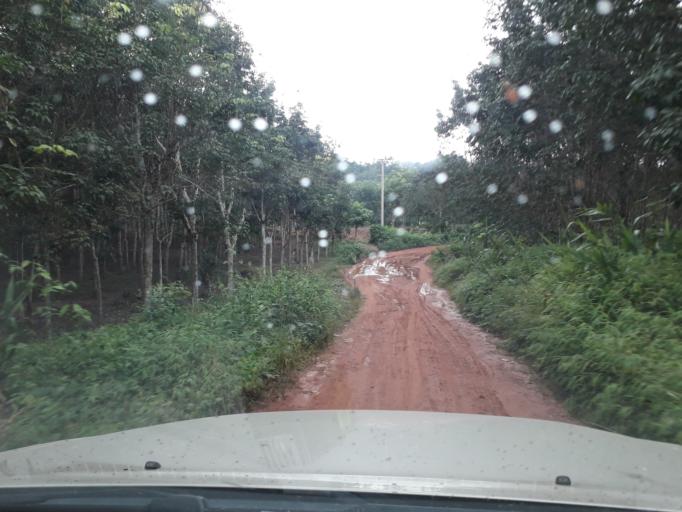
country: LA
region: Phongsali
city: Phongsali
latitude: 21.3049
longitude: 101.9748
